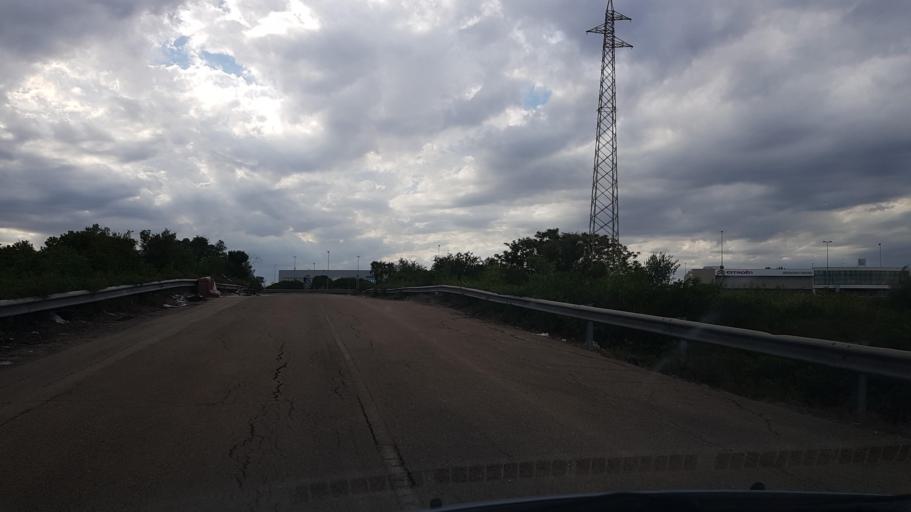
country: IT
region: Apulia
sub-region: Provincia di Taranto
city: Paolo VI
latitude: 40.5138
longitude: 17.2540
